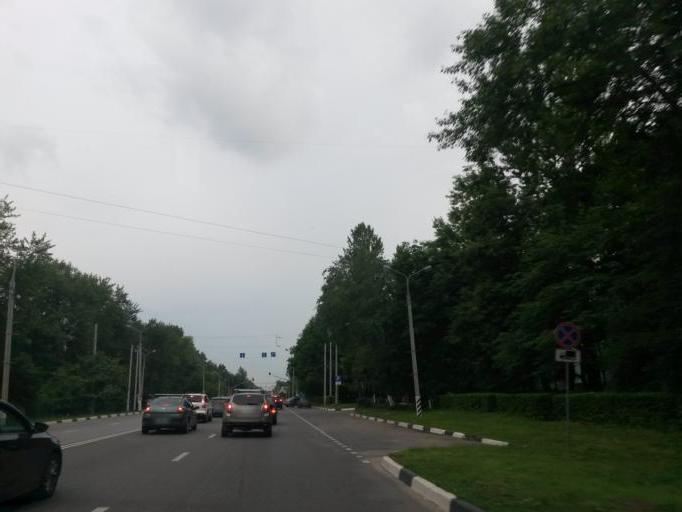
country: RU
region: Moskovskaya
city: Domodedovo
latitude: 55.4260
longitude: 37.7723
